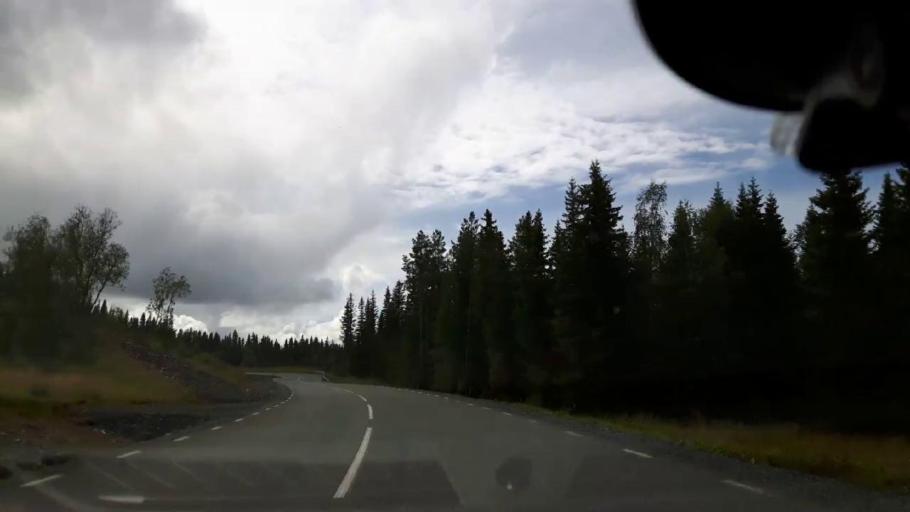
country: SE
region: Jaemtland
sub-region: Krokoms Kommun
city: Valla
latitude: 63.4878
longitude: 13.8639
